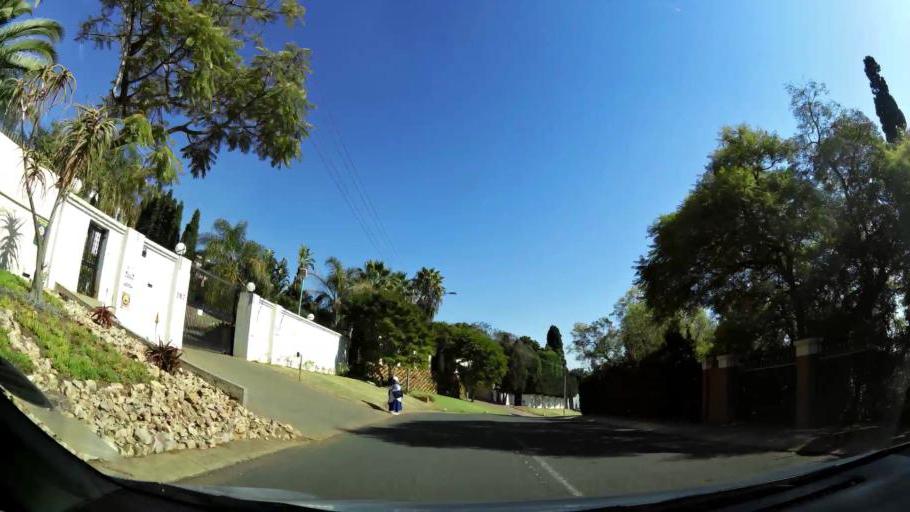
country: ZA
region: Gauteng
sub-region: City of Tshwane Metropolitan Municipality
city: Pretoria
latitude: -25.7803
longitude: 28.2227
